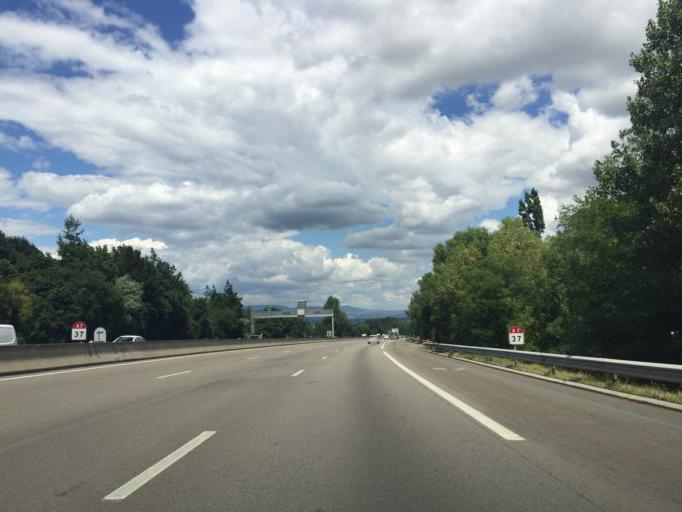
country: FR
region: Rhone-Alpes
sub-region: Departement de la Drome
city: Saint-Uze
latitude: 45.2142
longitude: 4.8619
